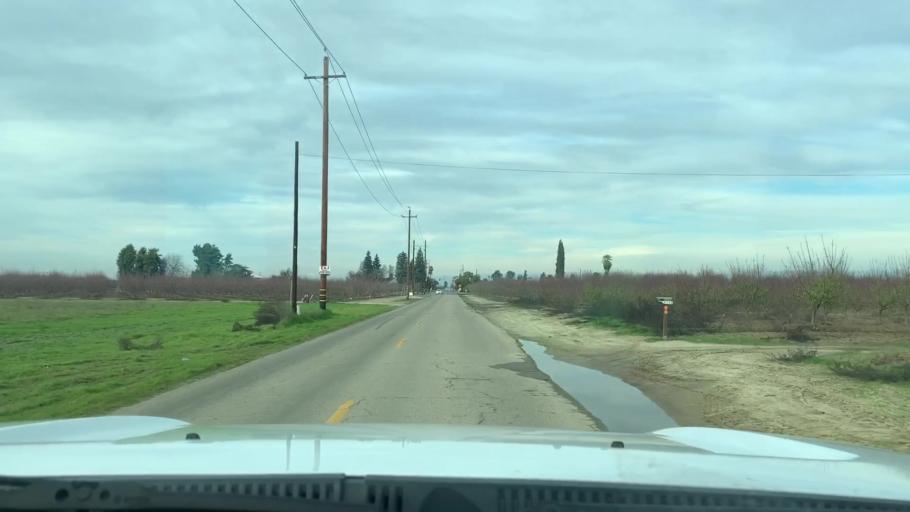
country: US
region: California
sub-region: Fresno County
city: Selma
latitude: 36.6007
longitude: -119.5748
